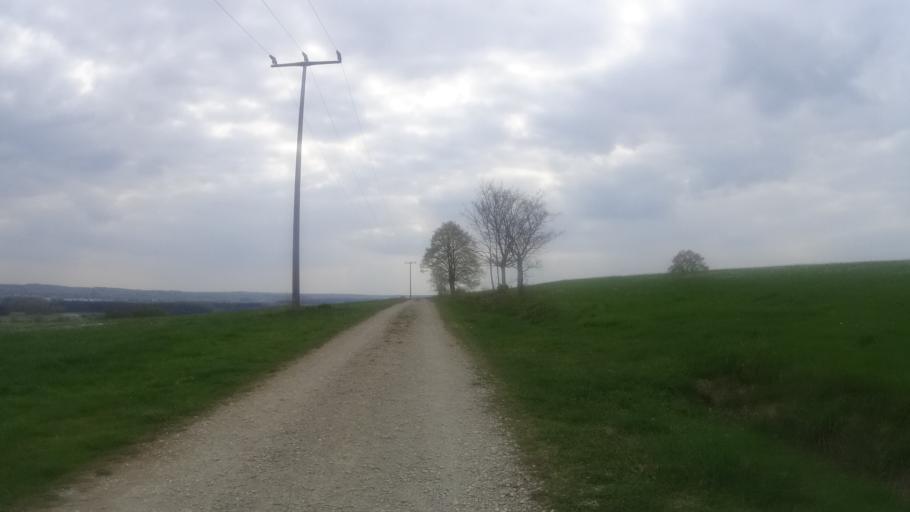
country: DE
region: Bavaria
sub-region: Upper Franconia
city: Igensdorf
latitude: 49.6035
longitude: 11.2138
